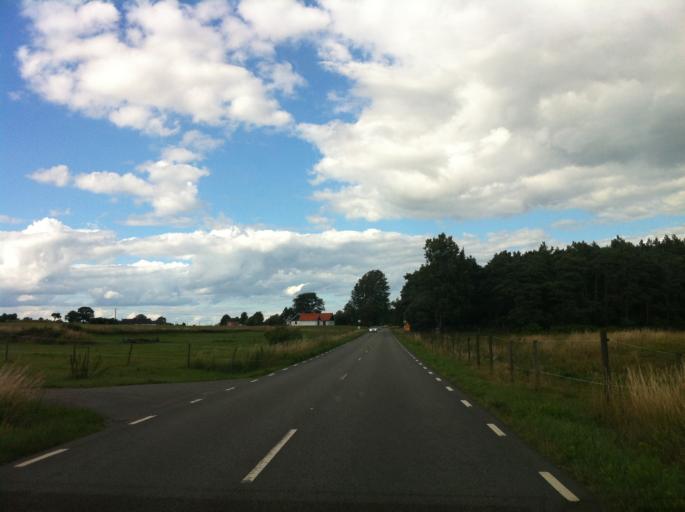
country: SE
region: Skane
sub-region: Simrishamns Kommun
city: Simrishamn
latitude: 55.4181
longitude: 14.2094
